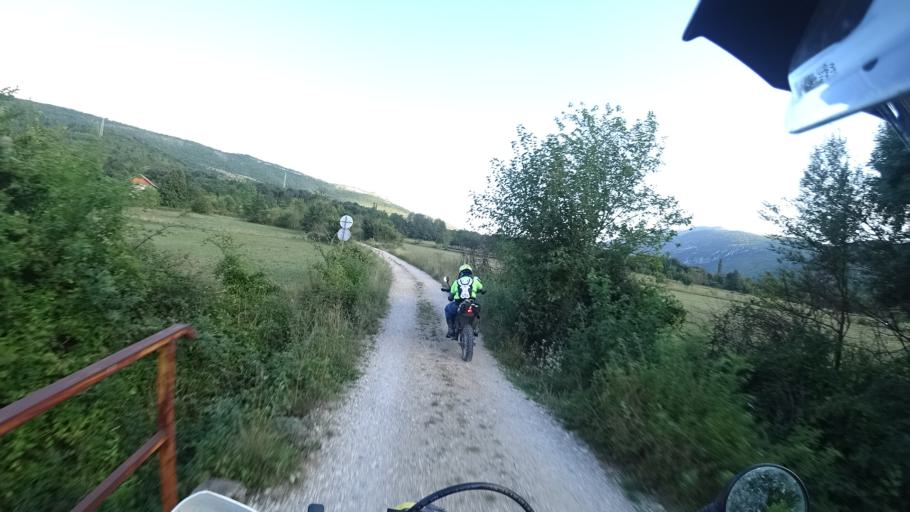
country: HR
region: Sibensko-Kniniska
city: Knin
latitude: 44.1923
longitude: 16.0578
